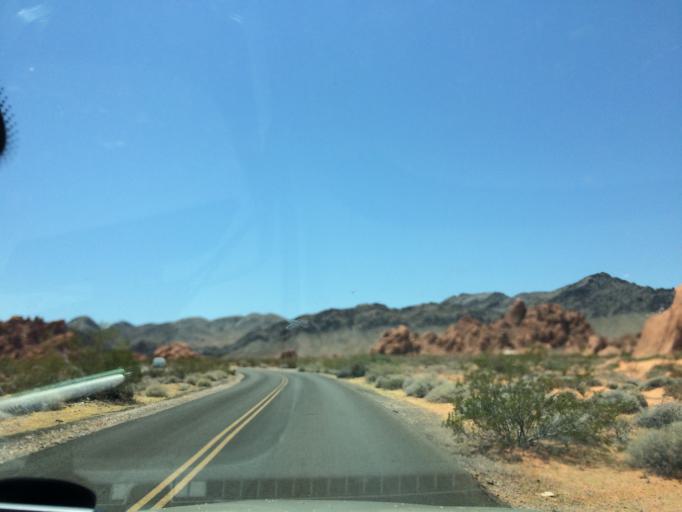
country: US
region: Nevada
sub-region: Clark County
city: Moapa Valley
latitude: 36.4230
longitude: -114.5498
